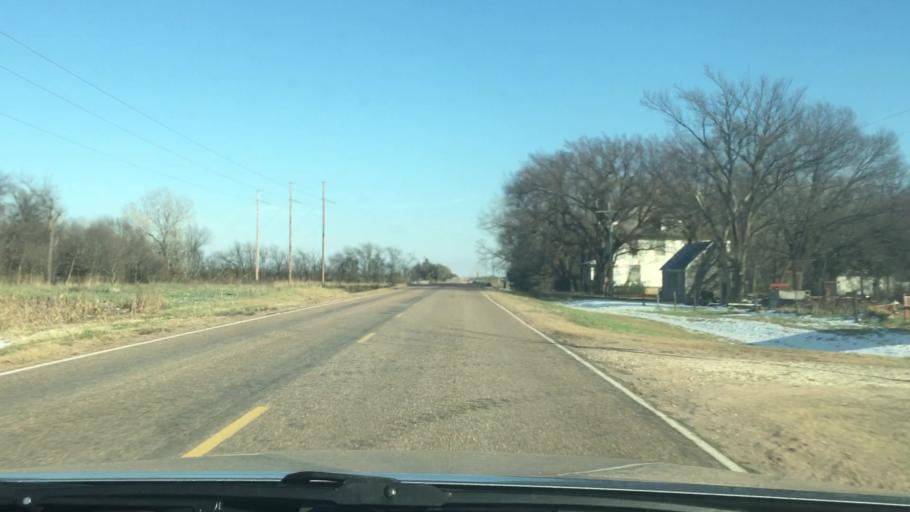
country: US
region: Kansas
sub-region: Rice County
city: Lyons
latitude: 38.2895
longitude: -98.1225
